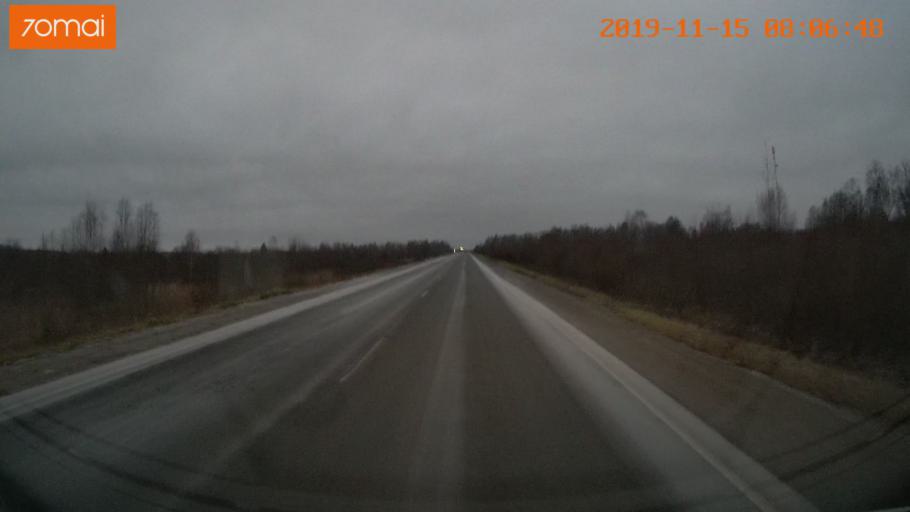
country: RU
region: Vologda
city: Cherepovets
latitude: 59.0236
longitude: 38.0297
